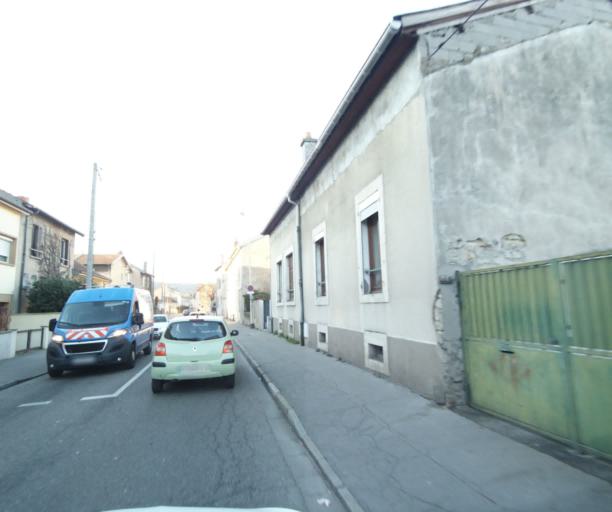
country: FR
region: Lorraine
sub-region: Departement de Meurthe-et-Moselle
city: Maxeville
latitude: 48.7059
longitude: 6.1733
